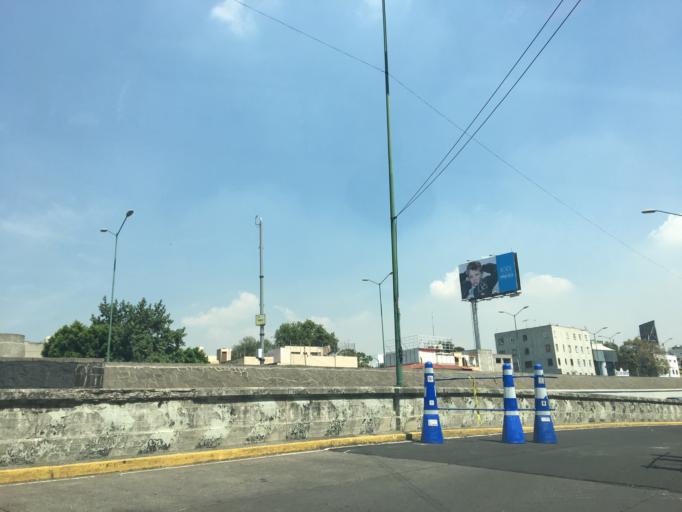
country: MX
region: Mexico City
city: Benito Juarez
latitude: 19.4011
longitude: -99.1653
